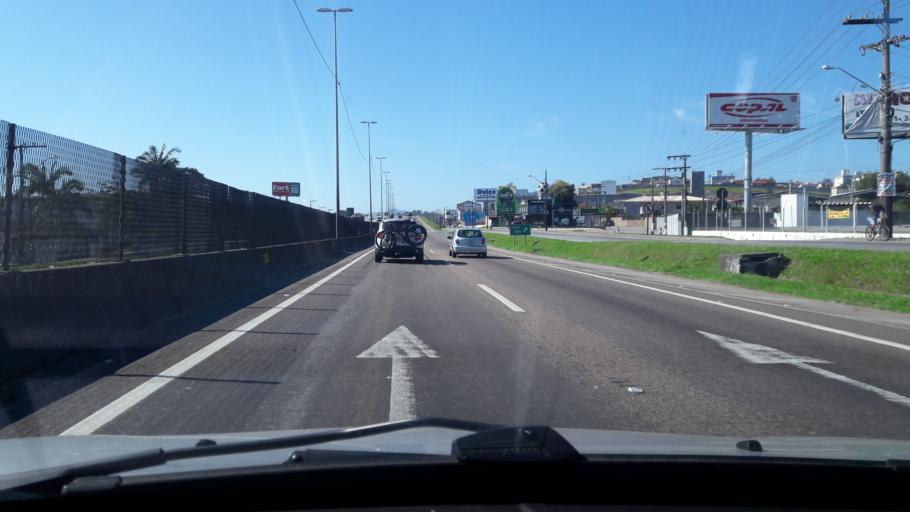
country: BR
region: Santa Catarina
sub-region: Biguacu
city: Biguacu
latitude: -27.5355
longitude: -48.6282
